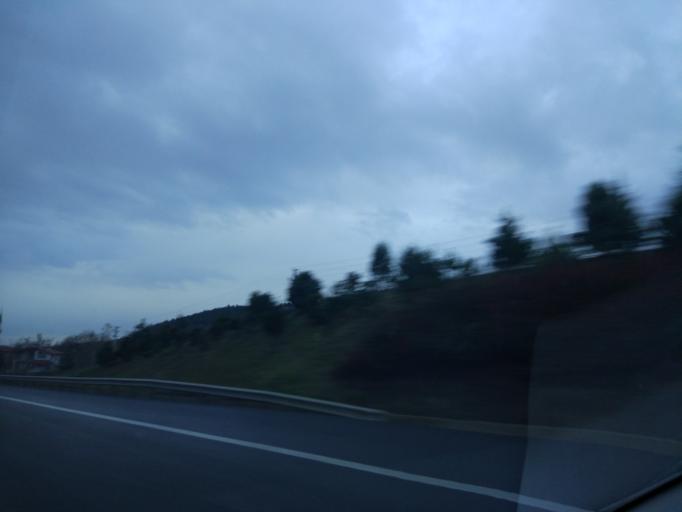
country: TR
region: Duzce
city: Kaynasli
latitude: 40.7814
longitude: 31.3388
